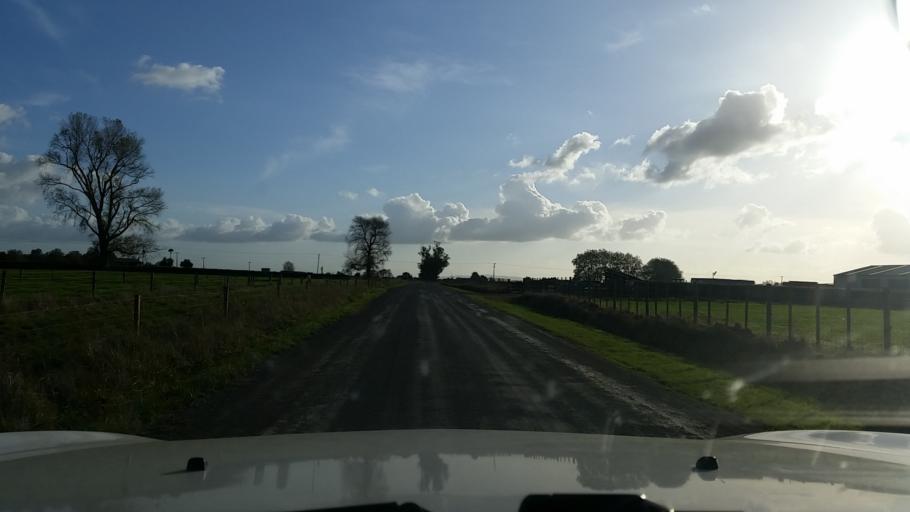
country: NZ
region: Bay of Plenty
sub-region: Western Bay of Plenty District
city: Katikati
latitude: -37.5775
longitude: 175.7260
